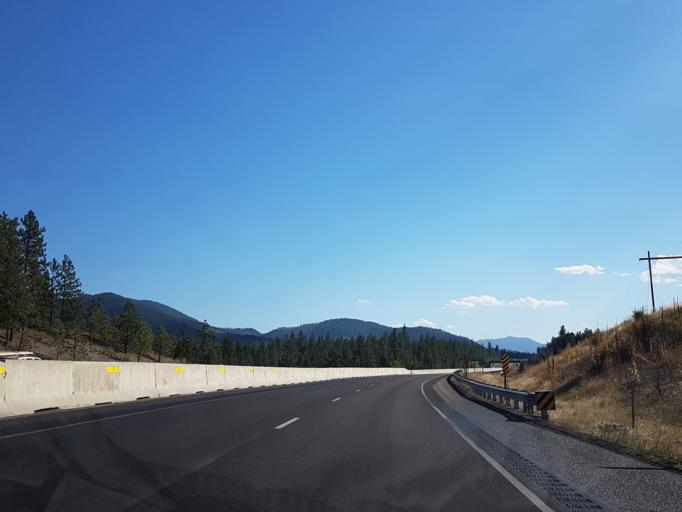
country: US
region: Montana
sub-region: Mineral County
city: Superior
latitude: 47.1332
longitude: -114.7982
